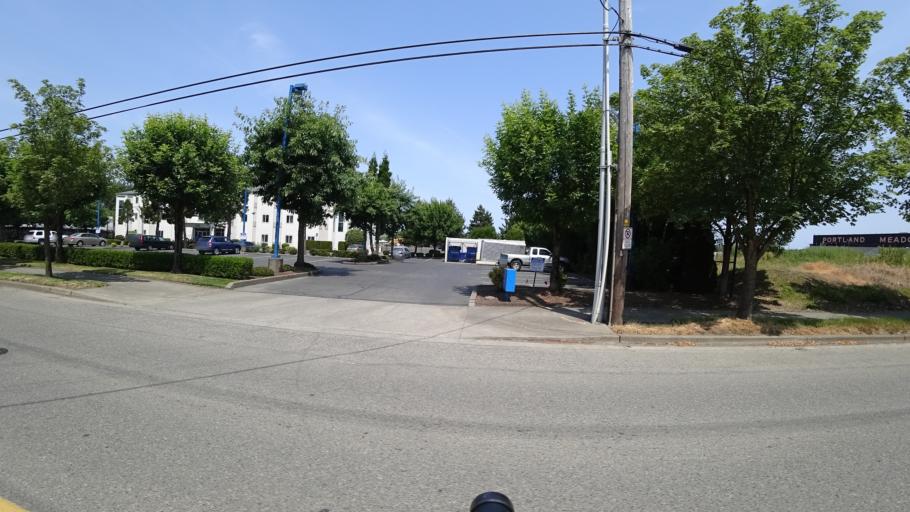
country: US
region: Washington
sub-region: Clark County
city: Vancouver
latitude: 45.5895
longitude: -122.6792
